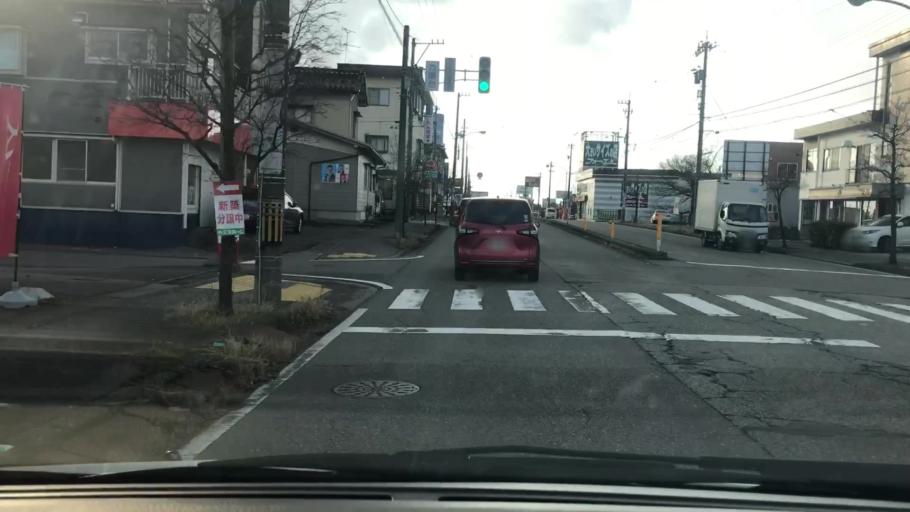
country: JP
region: Toyama
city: Toyama-shi
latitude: 36.6690
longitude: 137.2351
